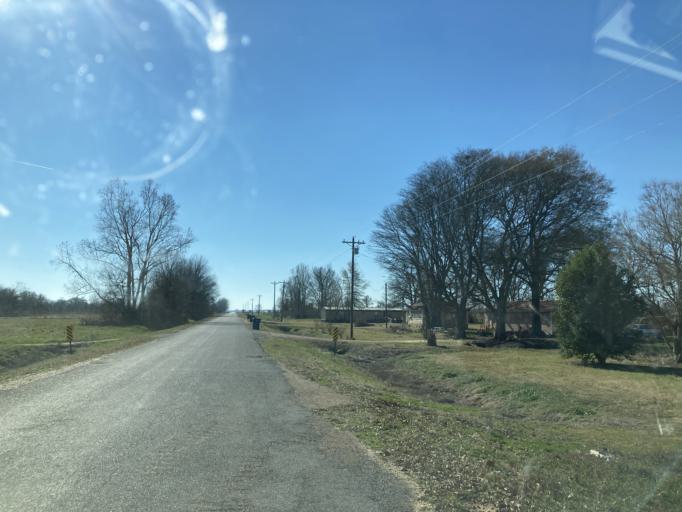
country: US
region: Mississippi
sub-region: Yazoo County
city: Yazoo City
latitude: 32.9689
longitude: -90.5958
